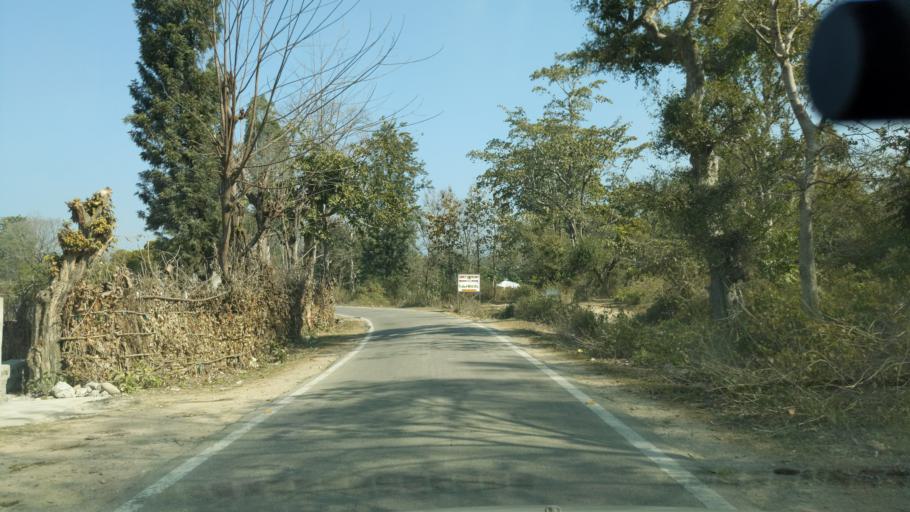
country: IN
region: Uttarakhand
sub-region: Naini Tal
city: Ramnagar
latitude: 29.4203
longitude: 79.1387
